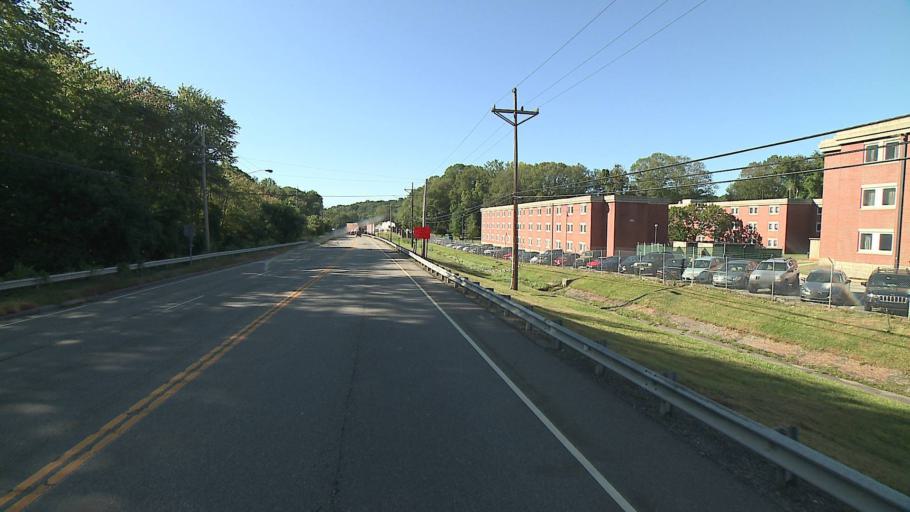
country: US
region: Connecticut
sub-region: New London County
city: Conning Towers-Nautilus Park
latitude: 41.3945
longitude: -72.0807
